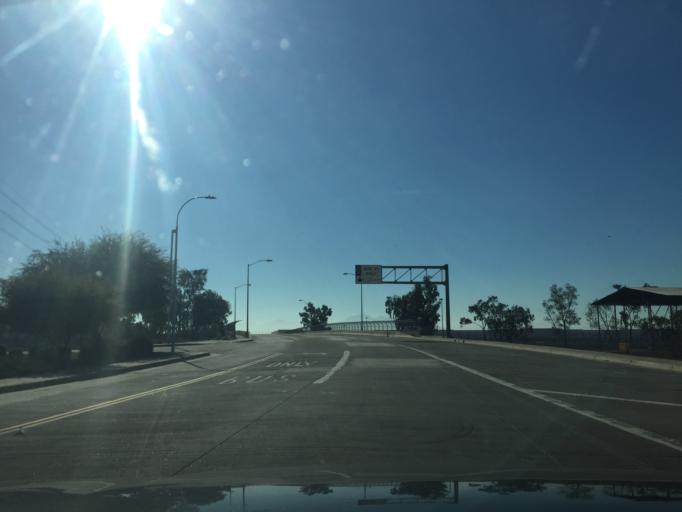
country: US
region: Arizona
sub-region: Maricopa County
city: Tolleson
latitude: 33.4640
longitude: -112.2295
